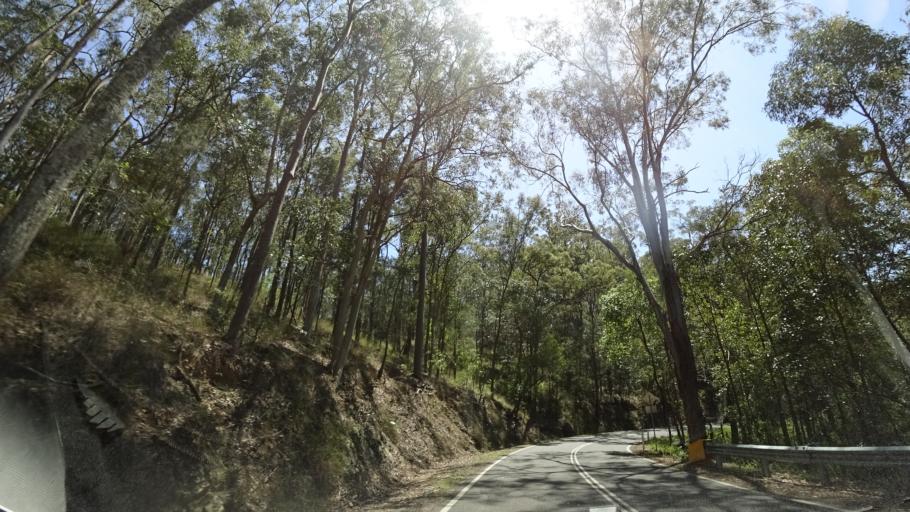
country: AU
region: Queensland
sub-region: Moreton Bay
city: Ferny Hills
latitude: -27.4344
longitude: 152.9233
